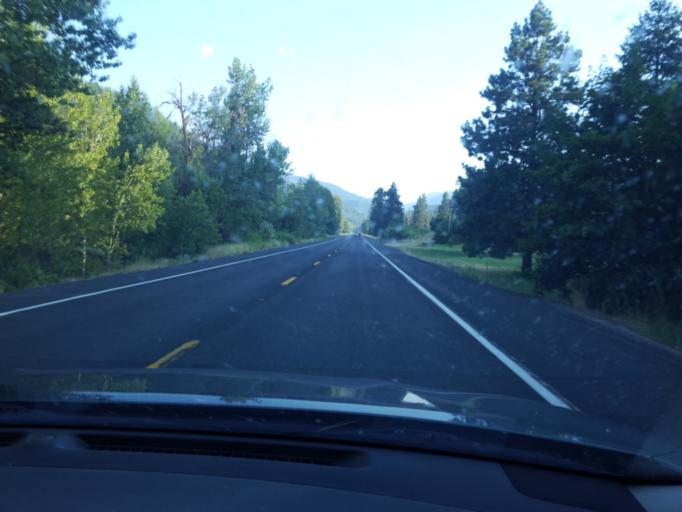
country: US
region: Washington
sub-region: Chelan County
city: Leavenworth
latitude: 47.5378
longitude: -120.6198
